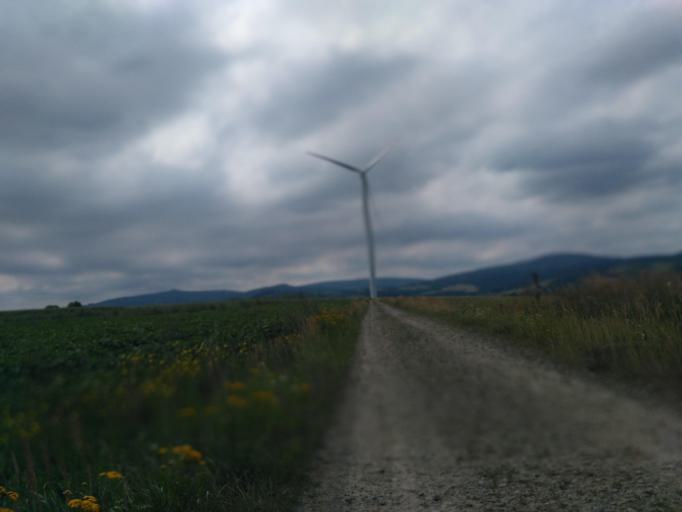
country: PL
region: Subcarpathian Voivodeship
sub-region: Powiat krosnienski
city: Rymanow
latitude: 49.5996
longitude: 21.8477
